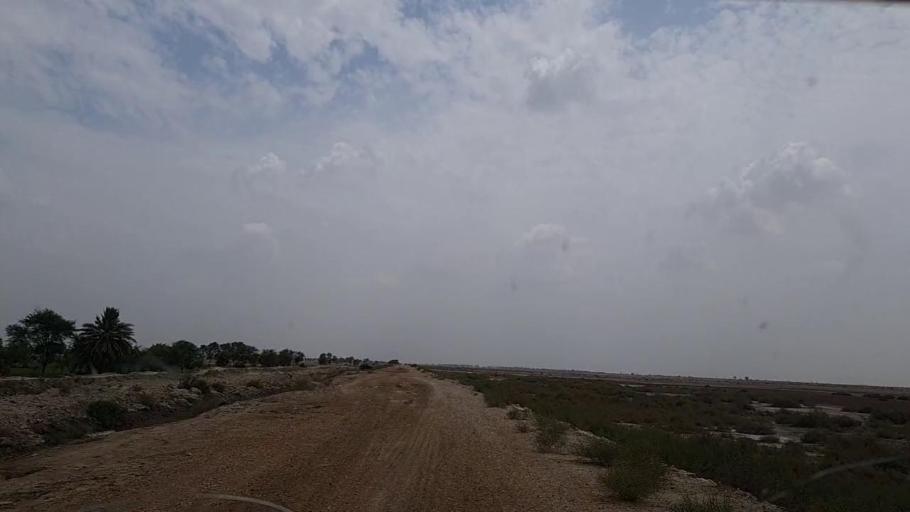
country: PK
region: Sindh
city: Johi
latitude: 26.7893
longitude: 67.6001
